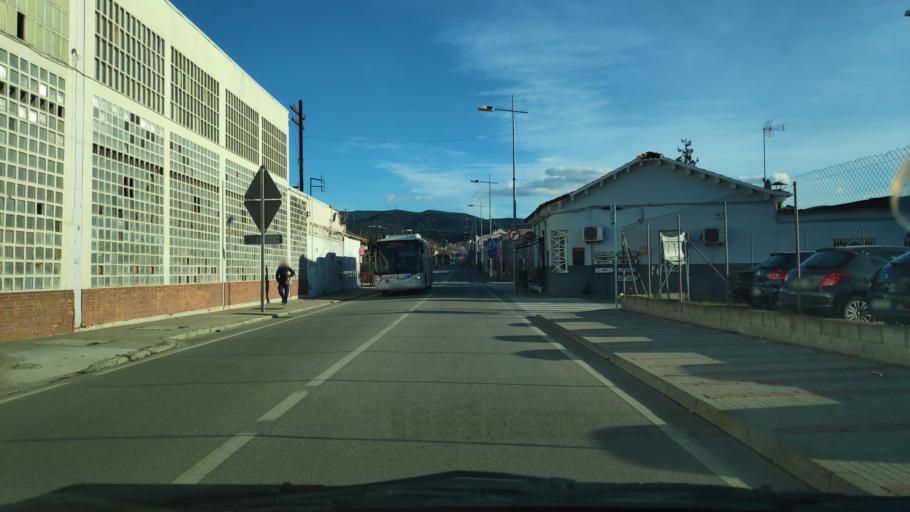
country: ES
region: Catalonia
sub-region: Provincia de Barcelona
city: Mollet del Valles
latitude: 41.5291
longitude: 2.2239
